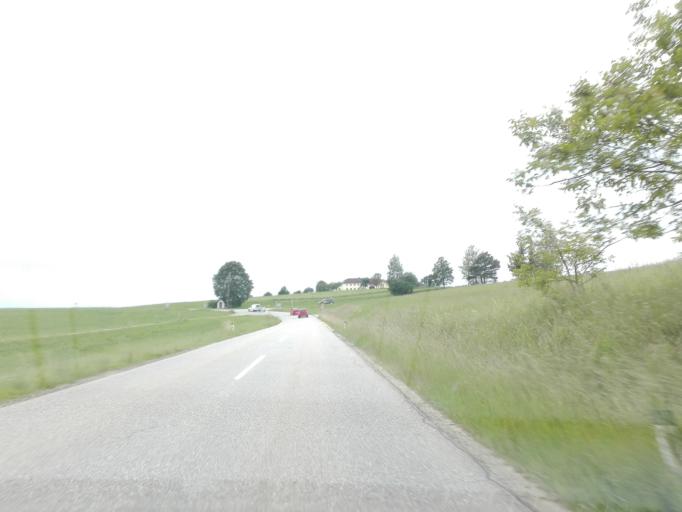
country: AT
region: Upper Austria
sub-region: Politischer Bezirk Perg
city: Bad Kreuzen
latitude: 48.2846
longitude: 14.7314
